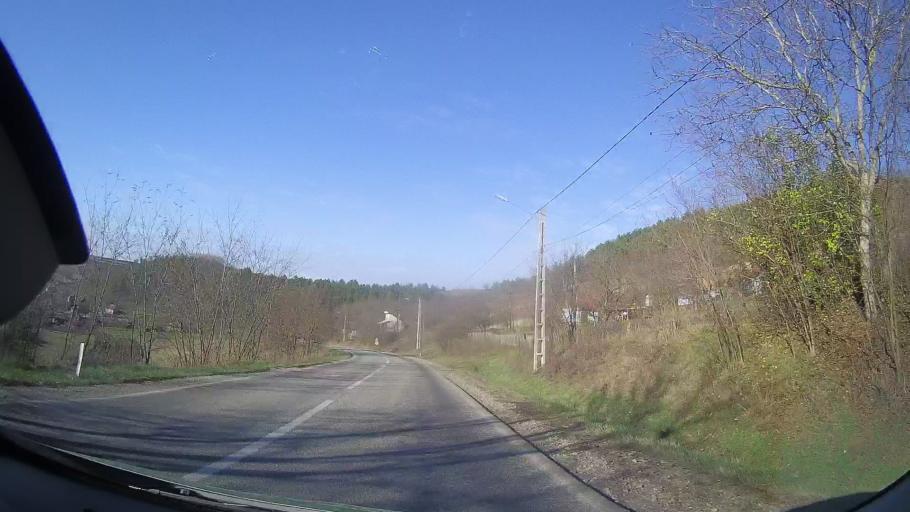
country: RO
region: Cluj
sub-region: Comuna Mociu
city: Mociu
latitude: 46.8033
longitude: 24.0453
